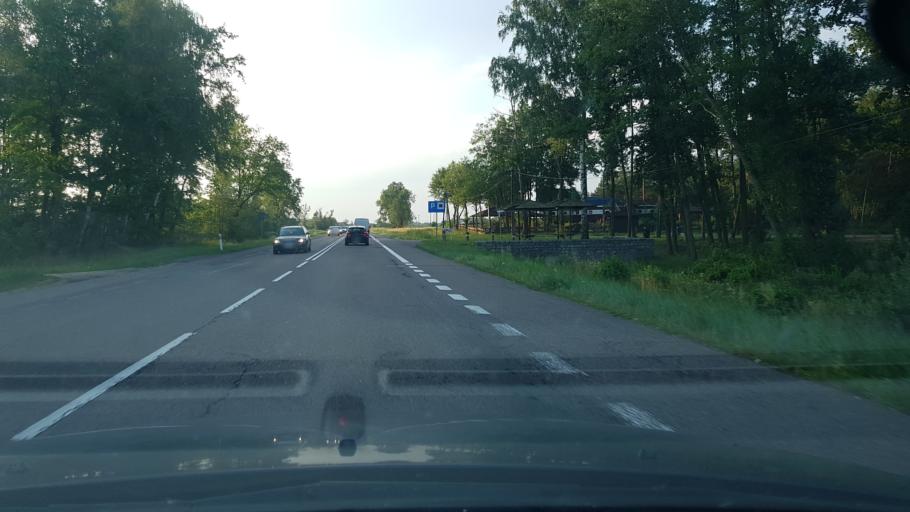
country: PL
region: Masovian Voivodeship
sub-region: Powiat plonski
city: Baboszewo
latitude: 52.7118
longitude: 20.3291
